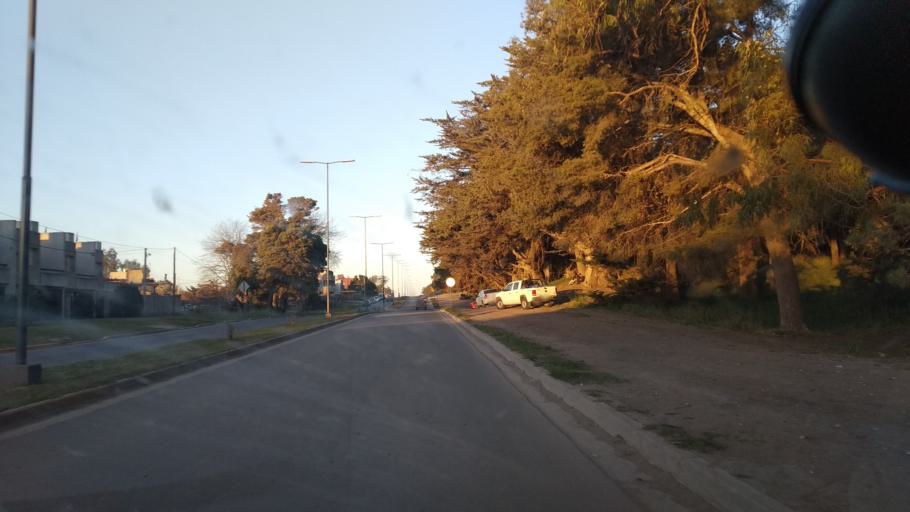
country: AR
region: Buenos Aires
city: Necochea
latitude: -38.5847
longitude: -58.7485
